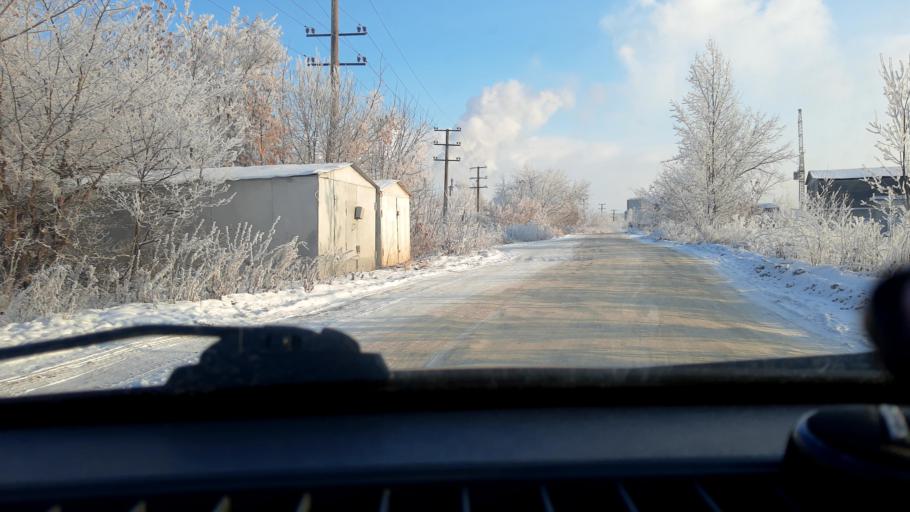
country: RU
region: Bashkortostan
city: Iglino
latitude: 54.7713
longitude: 56.2421
